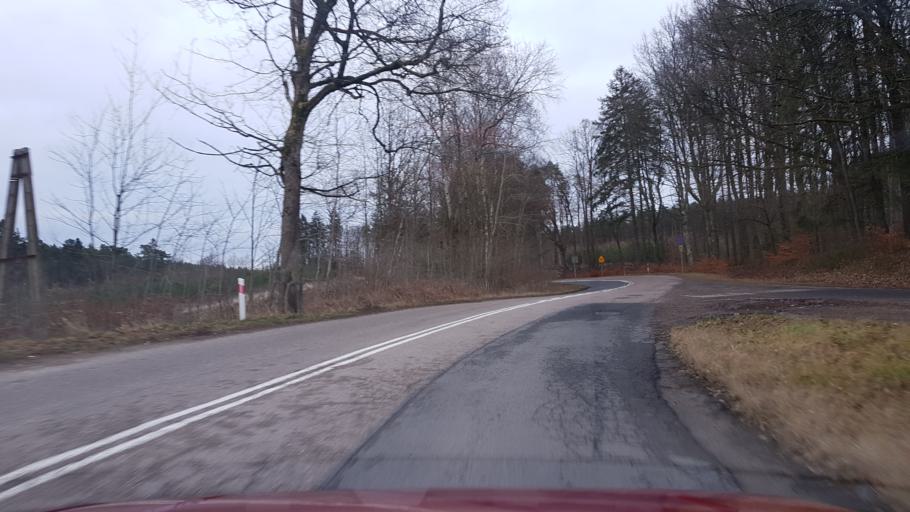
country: PL
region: West Pomeranian Voivodeship
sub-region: Powiat koszalinski
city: Sianow
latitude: 54.1874
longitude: 16.2599
